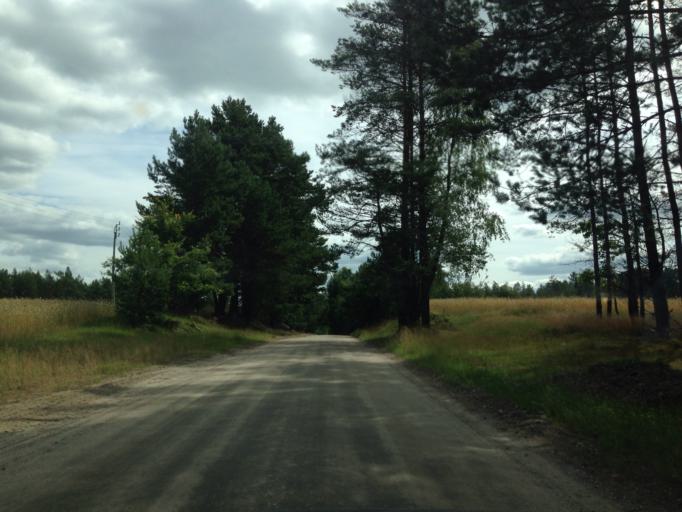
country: PL
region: Pomeranian Voivodeship
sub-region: Powiat koscierski
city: Lipusz
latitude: 54.0736
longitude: 17.7097
